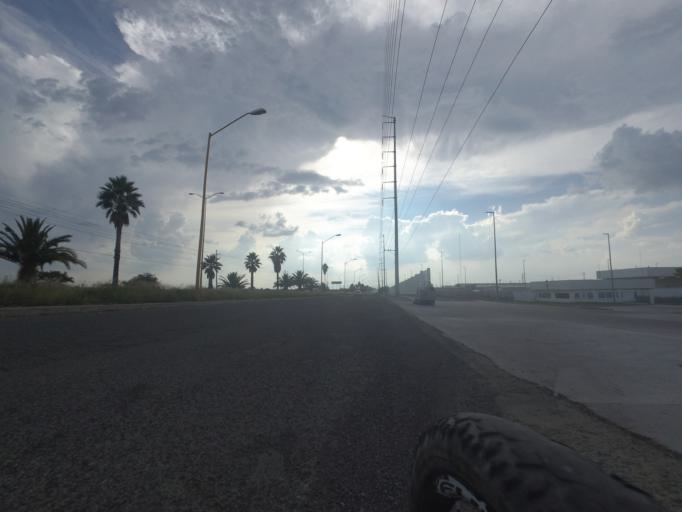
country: MX
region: Aguascalientes
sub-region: Aguascalientes
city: Penuelas (El Cienegal)
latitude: 21.7250
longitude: -102.2923
